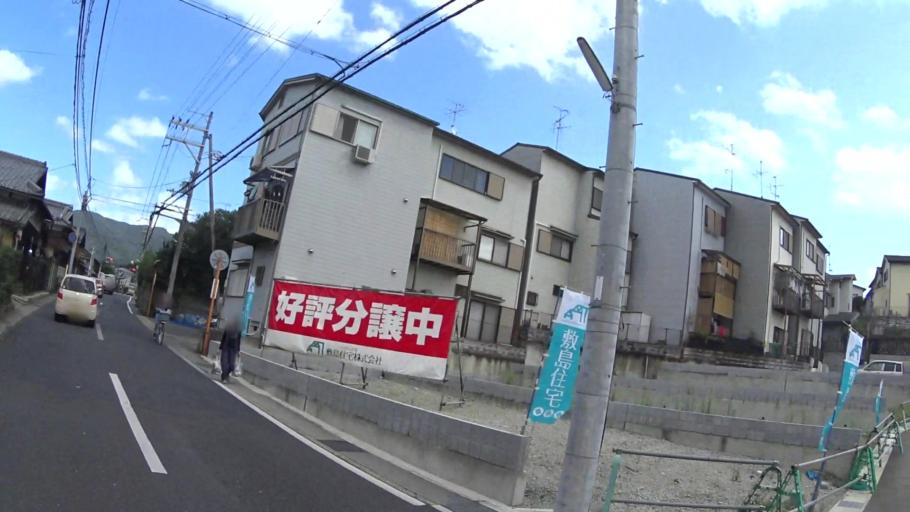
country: JP
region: Kyoto
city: Uji
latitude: 34.9379
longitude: 135.8063
